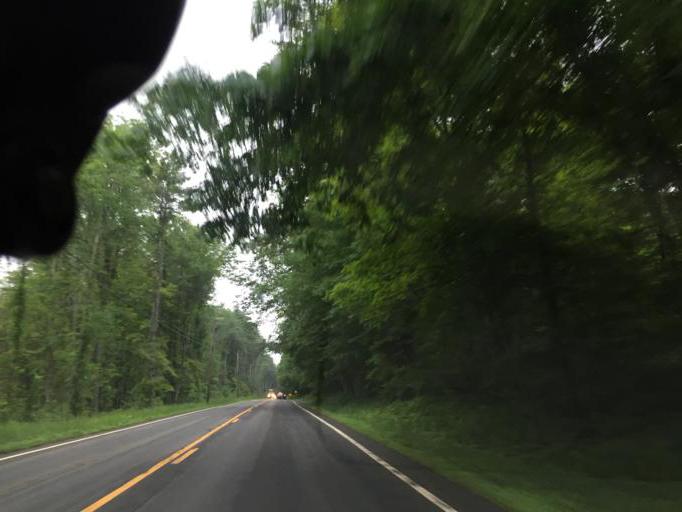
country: US
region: Connecticut
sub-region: Litchfield County
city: Canaan
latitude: 41.9443
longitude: -73.3122
